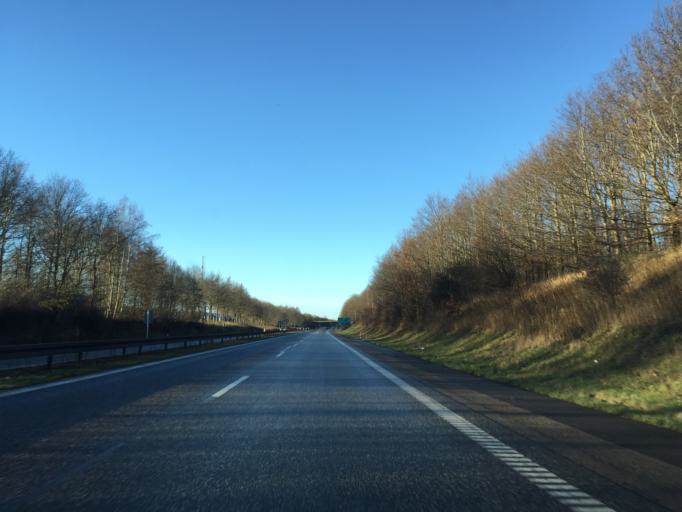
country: DK
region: South Denmark
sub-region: Odense Kommune
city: Bellinge
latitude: 55.3627
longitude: 10.3354
